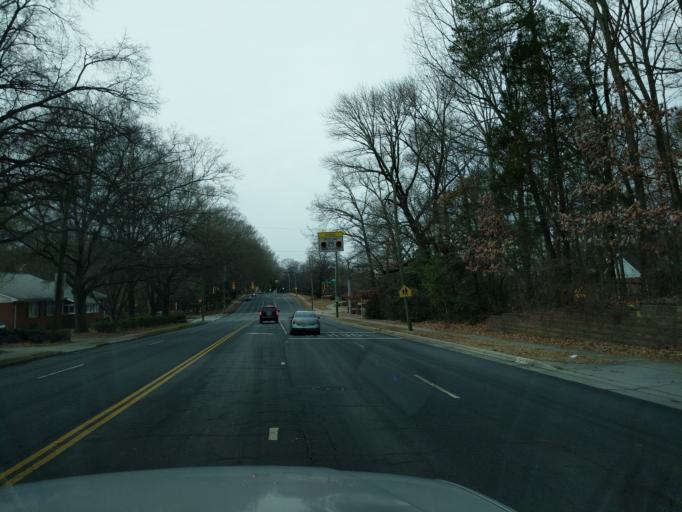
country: US
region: North Carolina
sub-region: Mecklenburg County
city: Charlotte
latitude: 35.1667
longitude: -80.8290
